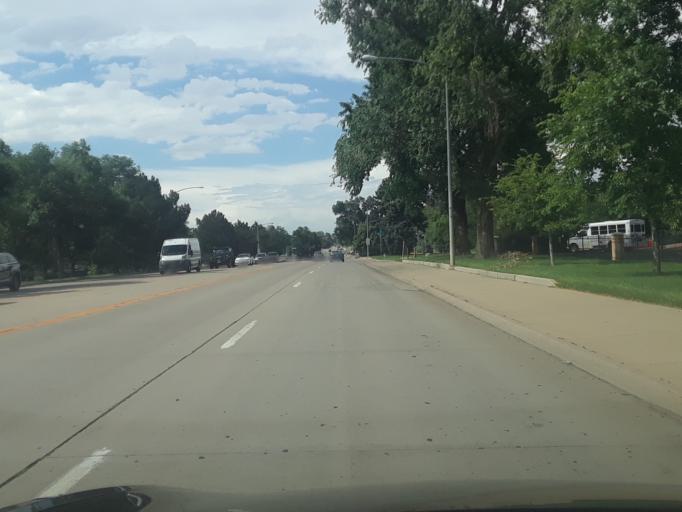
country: US
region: Colorado
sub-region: Arapahoe County
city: Glendale
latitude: 39.7223
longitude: -104.9034
